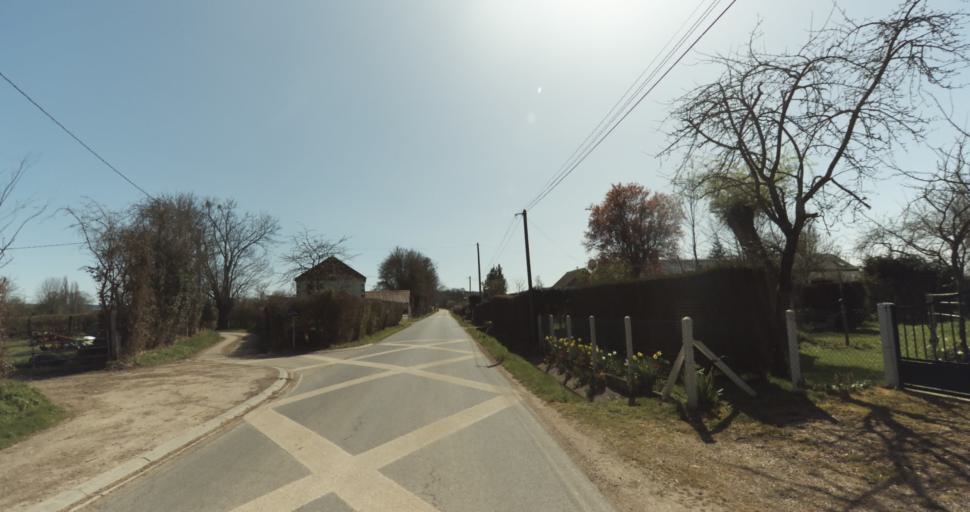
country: FR
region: Lower Normandy
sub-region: Departement du Calvados
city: Saint-Pierre-sur-Dives
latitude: 48.9700
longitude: -0.0056
